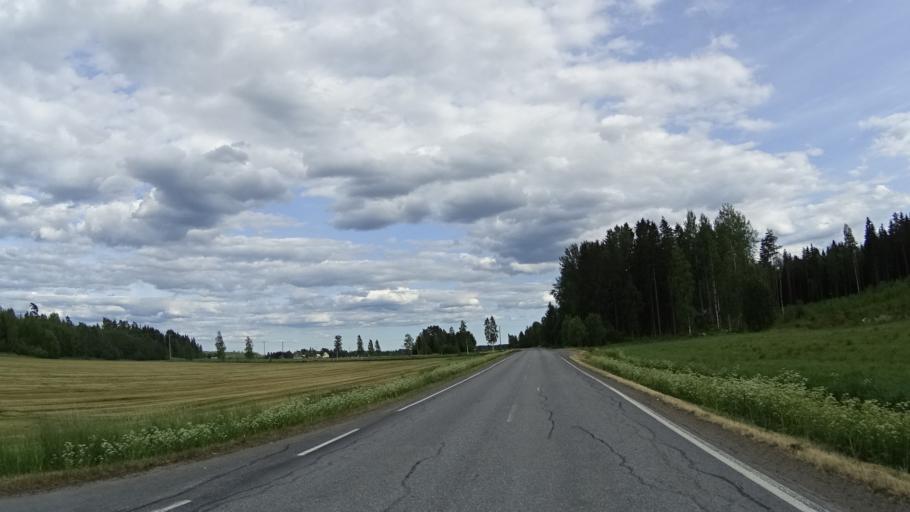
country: FI
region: Haeme
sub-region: Forssa
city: Forssa
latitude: 60.9405
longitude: 23.5566
